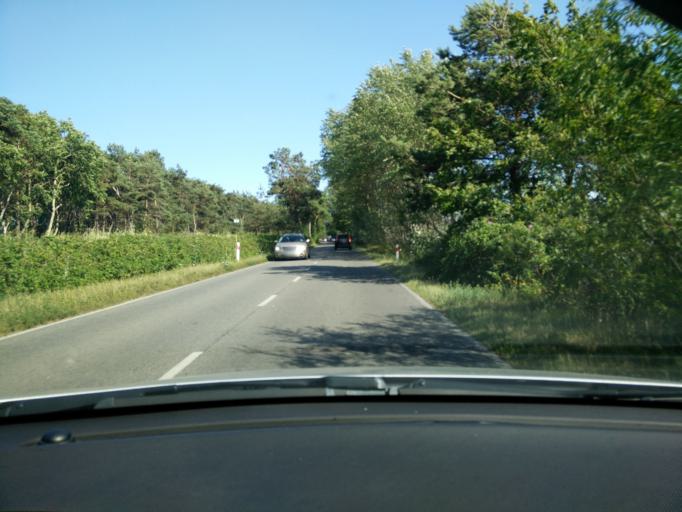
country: PL
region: Pomeranian Voivodeship
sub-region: Powiat pucki
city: Jastarnia
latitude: 54.7251
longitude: 18.6092
